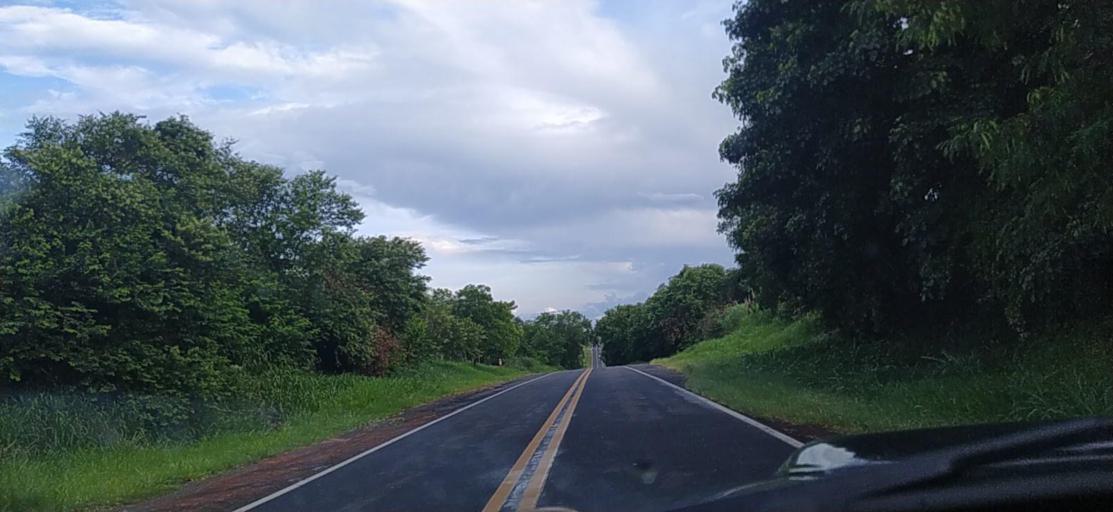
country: BR
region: Sao Paulo
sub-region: Pindorama
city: Pindorama
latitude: -21.1673
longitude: -48.9334
